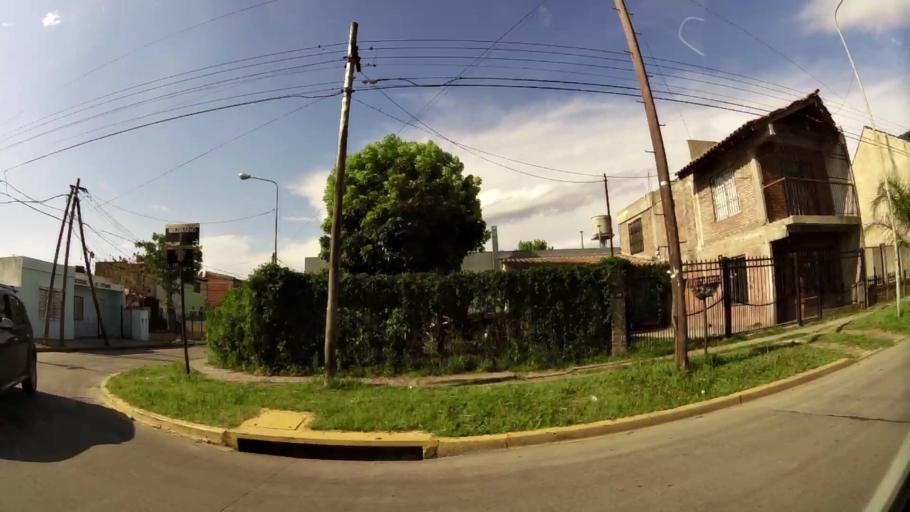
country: AR
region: Buenos Aires
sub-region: Partido de Merlo
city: Merlo
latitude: -34.6662
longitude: -58.7160
